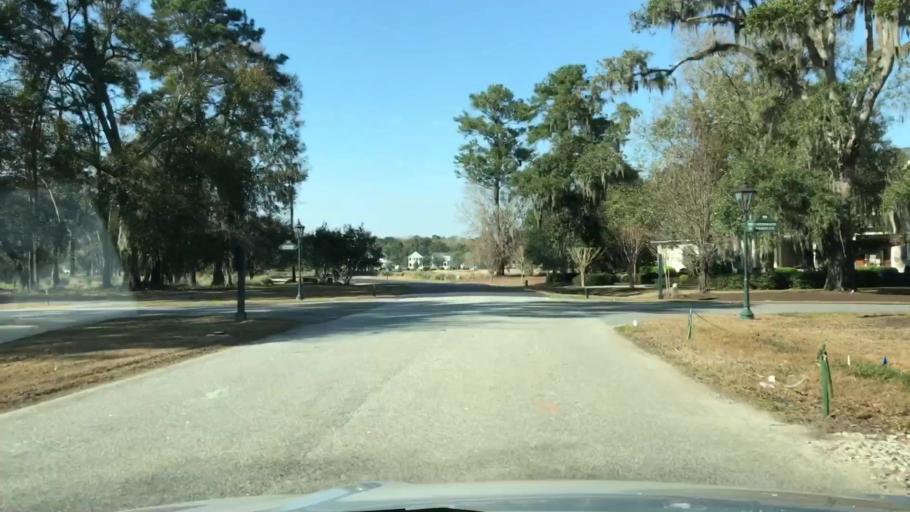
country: US
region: South Carolina
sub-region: Beaufort County
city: Bluffton
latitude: 32.3397
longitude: -80.9115
